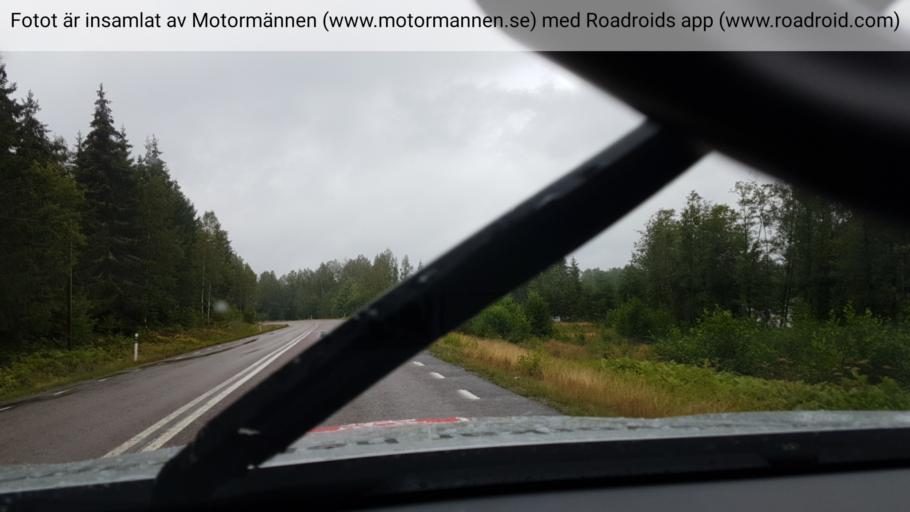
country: SE
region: Vaestra Goetaland
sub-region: Amals Kommun
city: Amal
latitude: 59.0751
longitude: 12.6341
